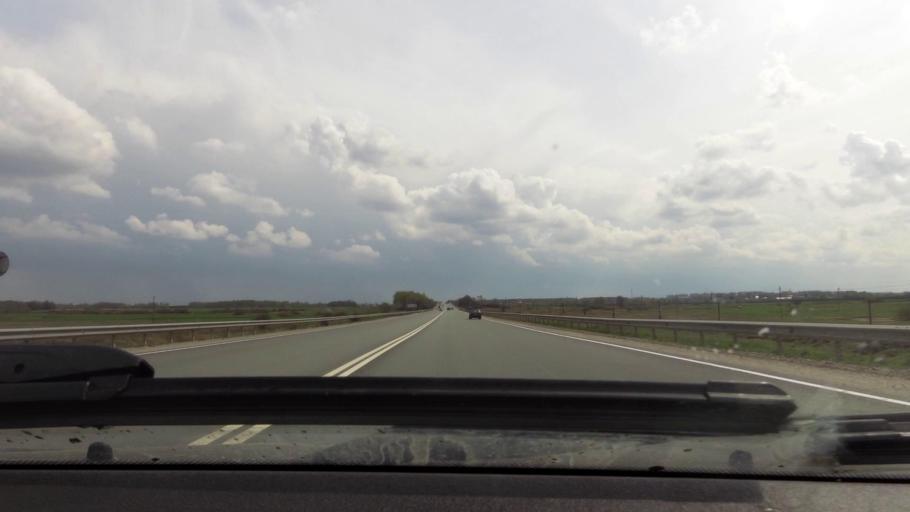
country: RU
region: Rjazan
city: Bagramovo
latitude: 54.7428
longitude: 39.4398
